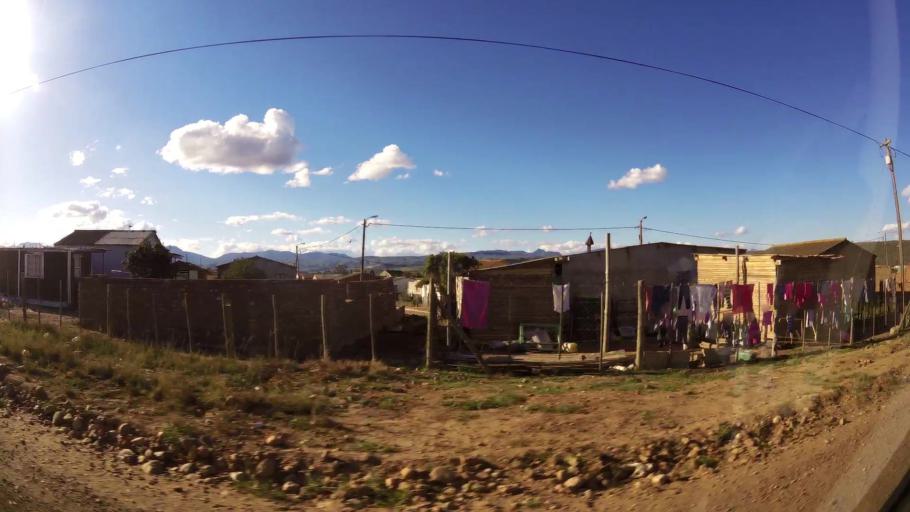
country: ZA
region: Western Cape
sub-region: Eden District Municipality
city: Riversdale
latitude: -34.1084
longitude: 20.9598
